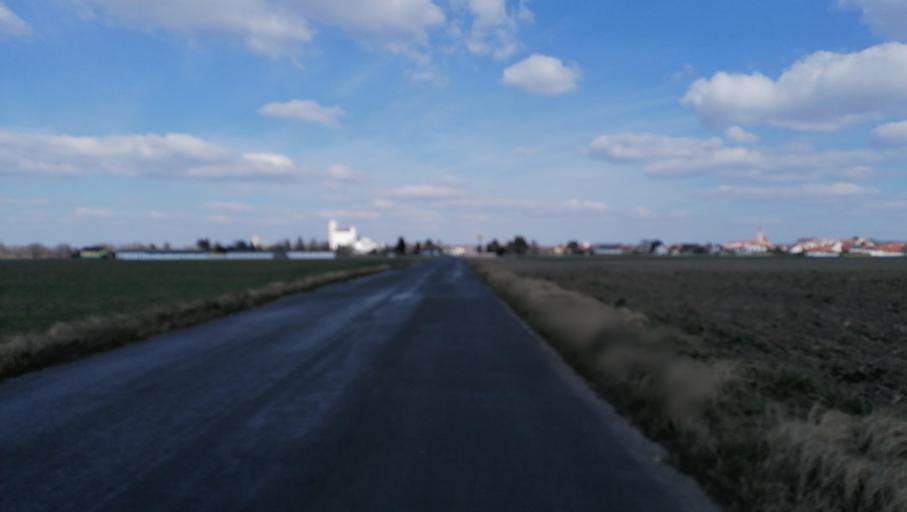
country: AT
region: Lower Austria
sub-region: Politischer Bezirk Wiener Neustadt
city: Lichtenworth
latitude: 47.8284
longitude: 16.2835
